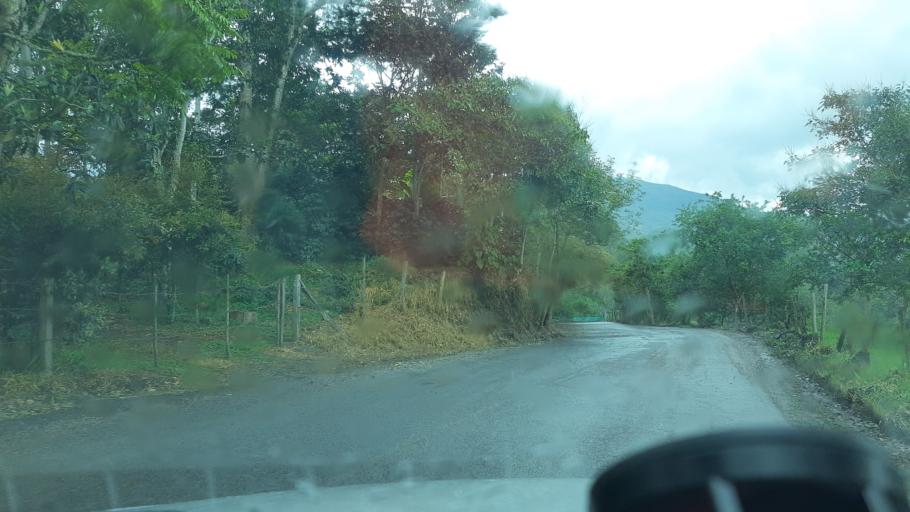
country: CO
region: Boyaca
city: Chinavita
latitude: 5.1524
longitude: -73.3639
